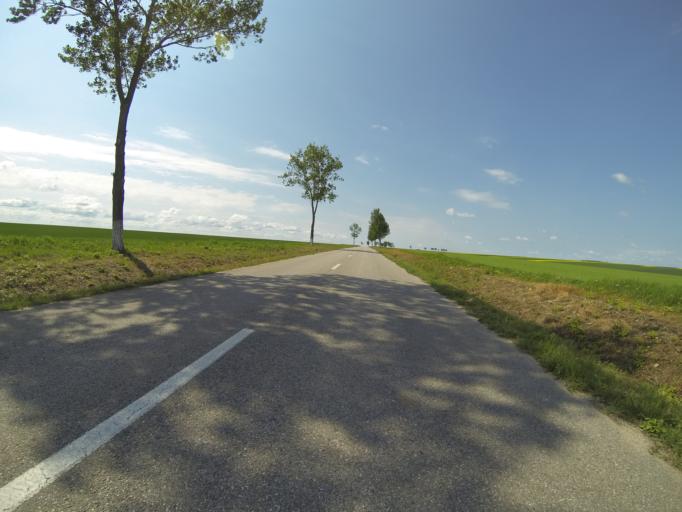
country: RO
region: Dolj
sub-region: Comuna Vartop
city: Vartop
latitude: 44.2173
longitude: 23.3141
